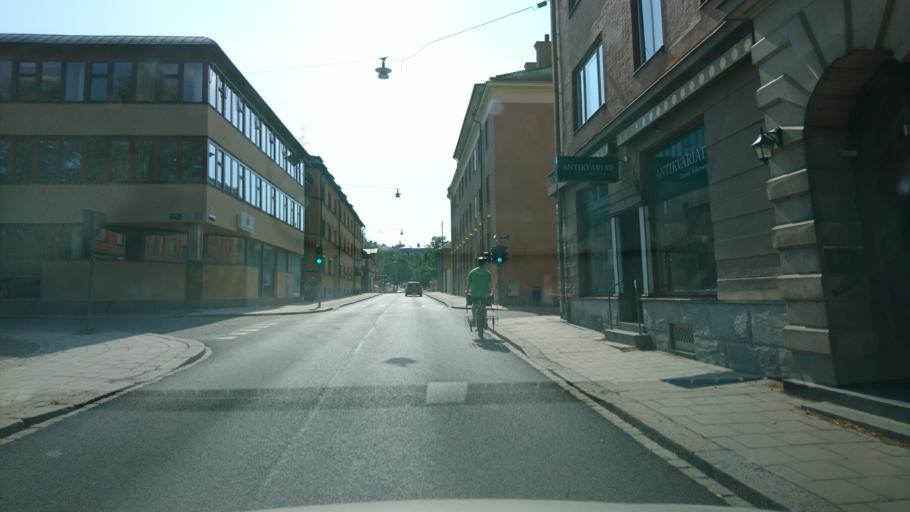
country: SE
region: Uppsala
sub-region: Uppsala Kommun
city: Uppsala
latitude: 59.8568
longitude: 17.6297
